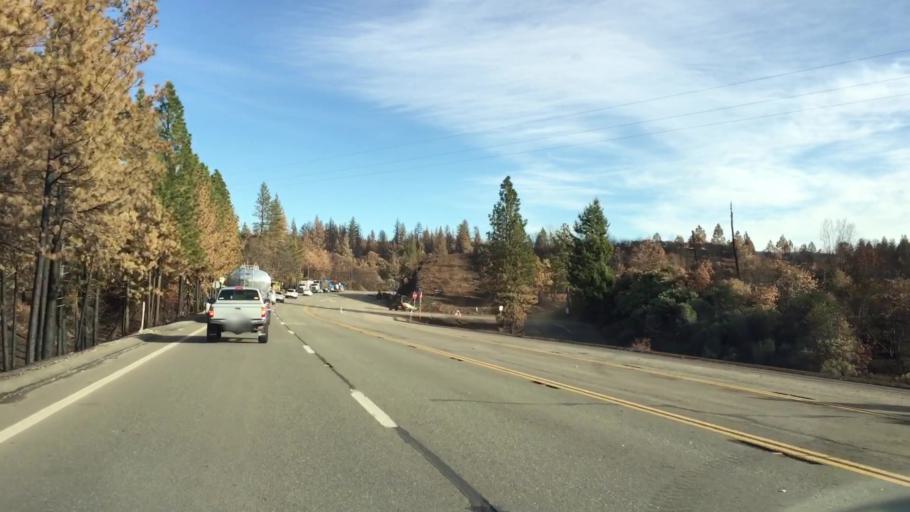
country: US
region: California
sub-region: Butte County
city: Paradise
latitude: 39.7148
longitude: -121.5219
